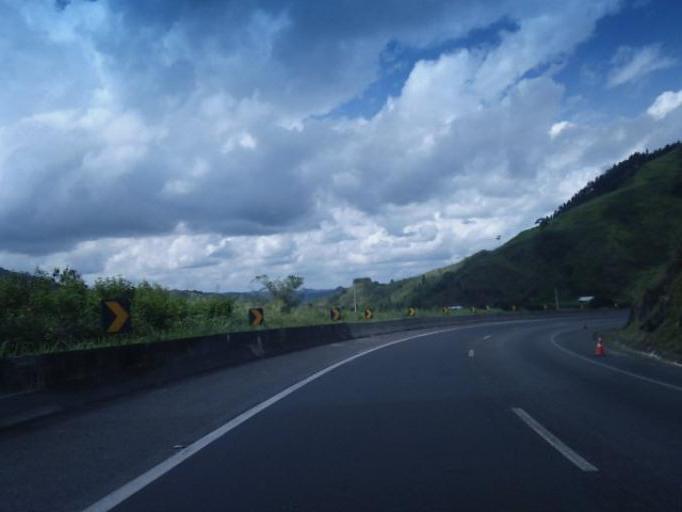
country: BR
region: Sao Paulo
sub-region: Cajati
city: Cajati
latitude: -24.8470
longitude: -48.2145
